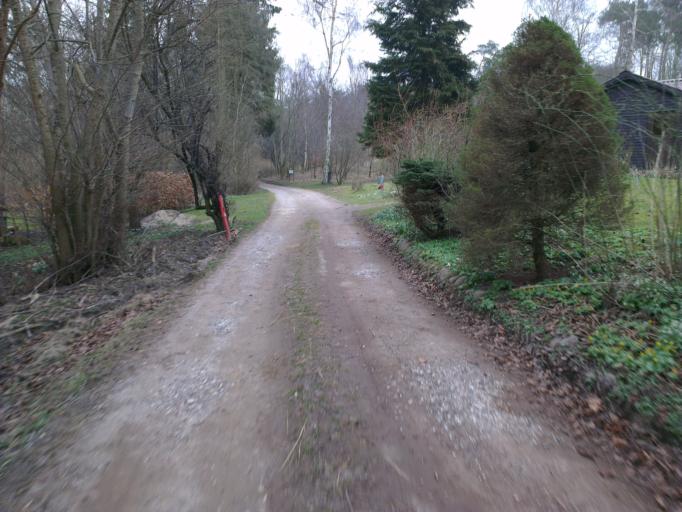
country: DK
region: Capital Region
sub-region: Frederikssund Kommune
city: Frederikssund
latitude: 55.7821
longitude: 12.0348
